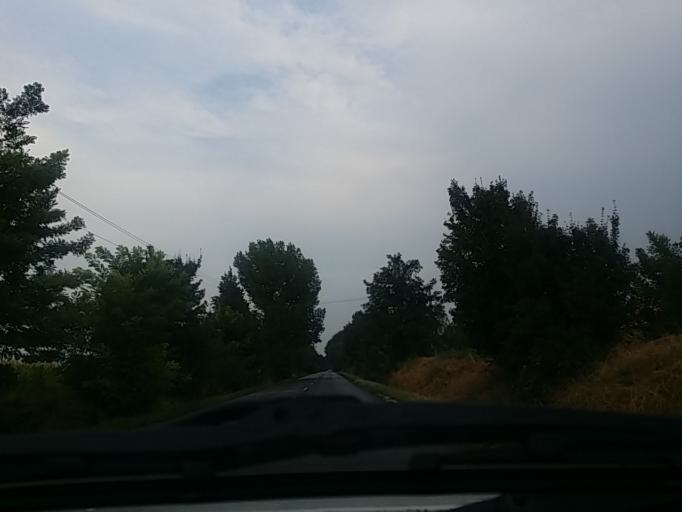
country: HU
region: Pest
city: Paty
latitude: 47.5138
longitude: 18.8091
